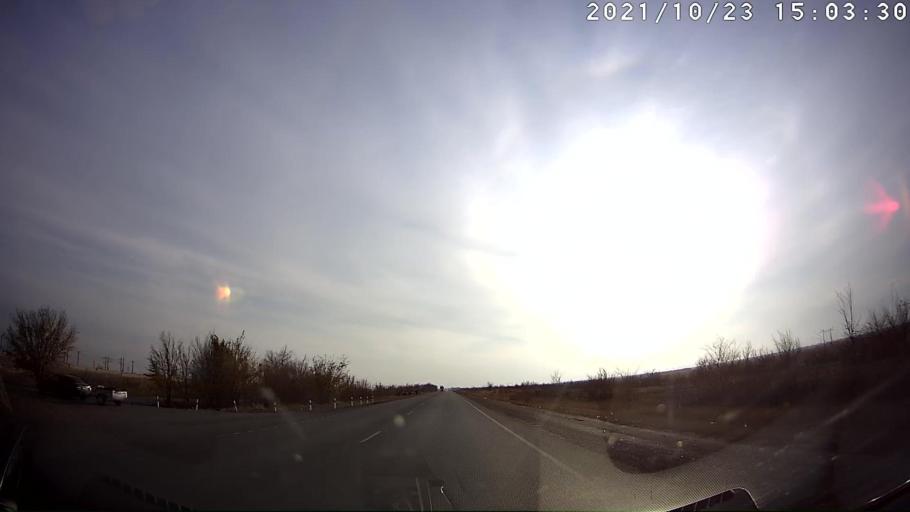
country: RU
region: Volgograd
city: Volgograd
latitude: 48.4122
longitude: 44.3762
